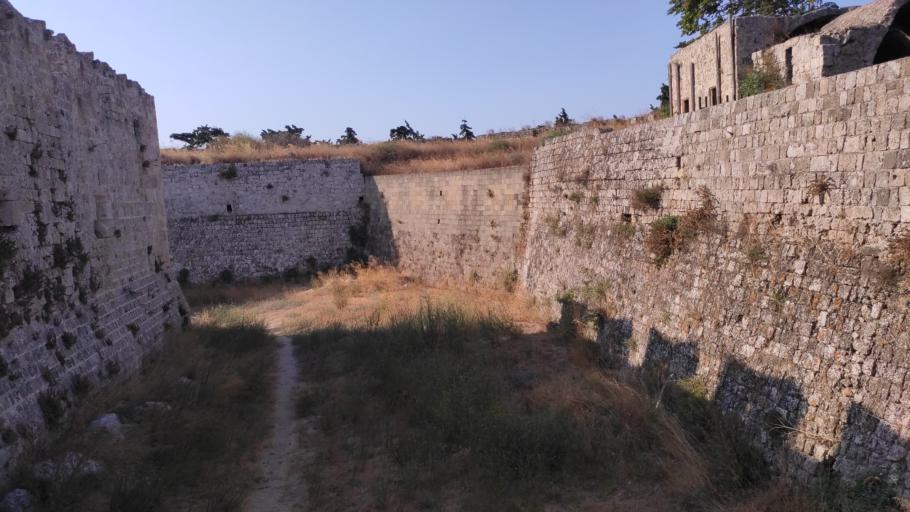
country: GR
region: South Aegean
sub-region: Nomos Dodekanisou
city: Rodos
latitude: 36.4399
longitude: 28.2281
